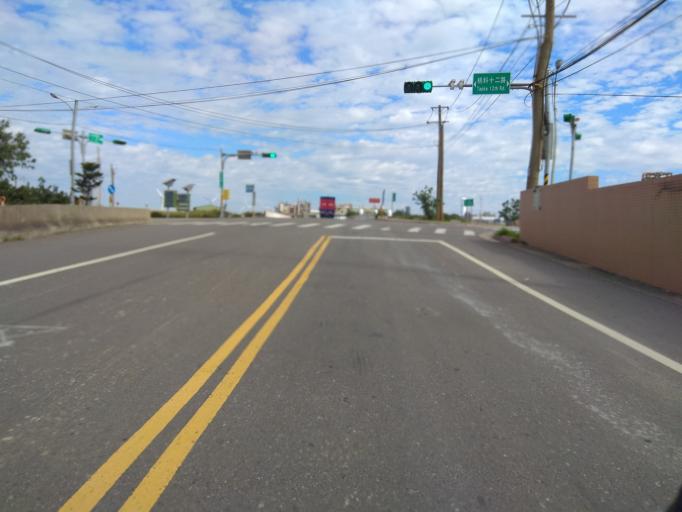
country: TW
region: Taiwan
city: Taoyuan City
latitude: 25.0545
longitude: 121.0994
